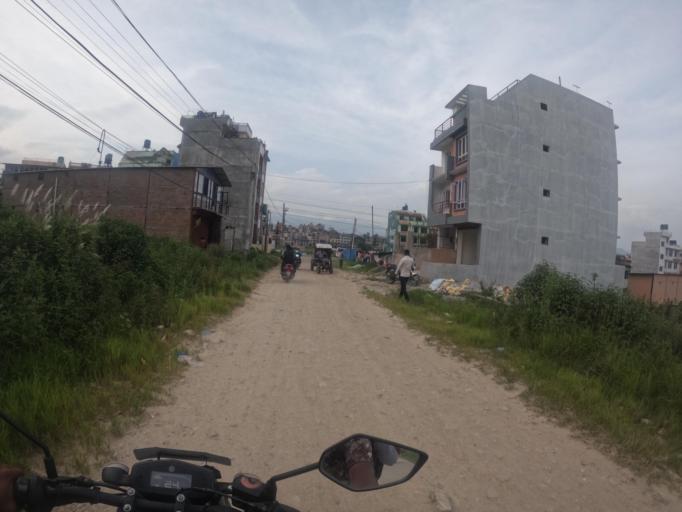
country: NP
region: Central Region
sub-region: Bagmati Zone
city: Bhaktapur
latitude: 27.6803
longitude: 85.3938
